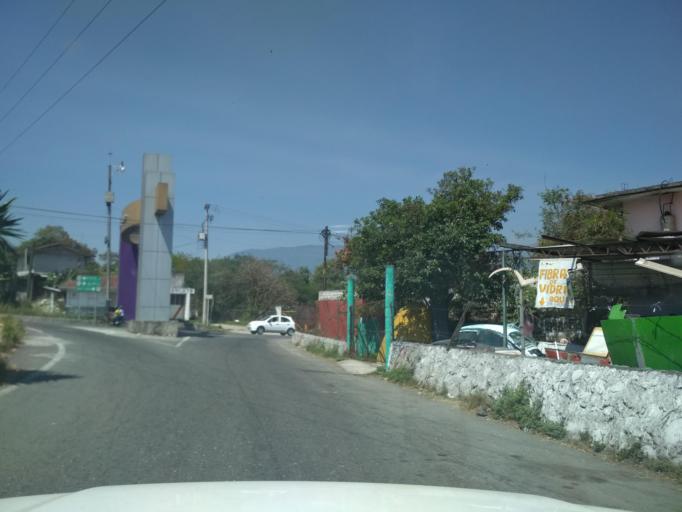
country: MX
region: Veracruz
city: Jalapilla
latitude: 18.8328
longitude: -97.0903
